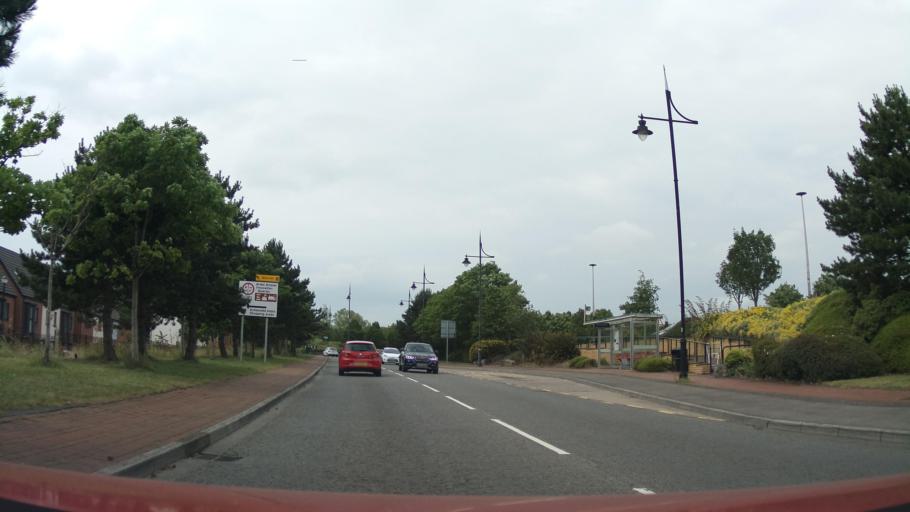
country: GB
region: Wales
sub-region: Vale of Glamorgan
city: Barry
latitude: 51.4010
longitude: -3.2719
